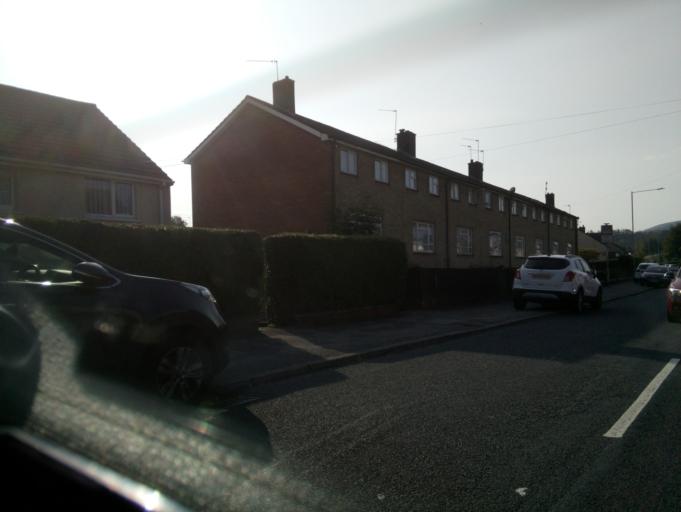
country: GB
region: Wales
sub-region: Newport
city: Newport
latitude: 51.6117
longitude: -3.0210
